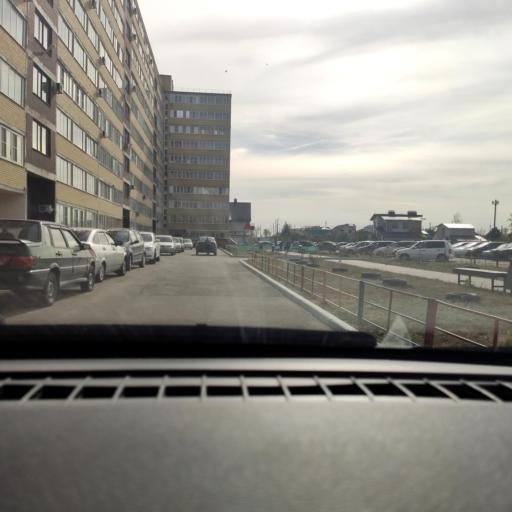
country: RU
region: Voronezj
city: Novaya Usman'
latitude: 51.6084
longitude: 39.3796
